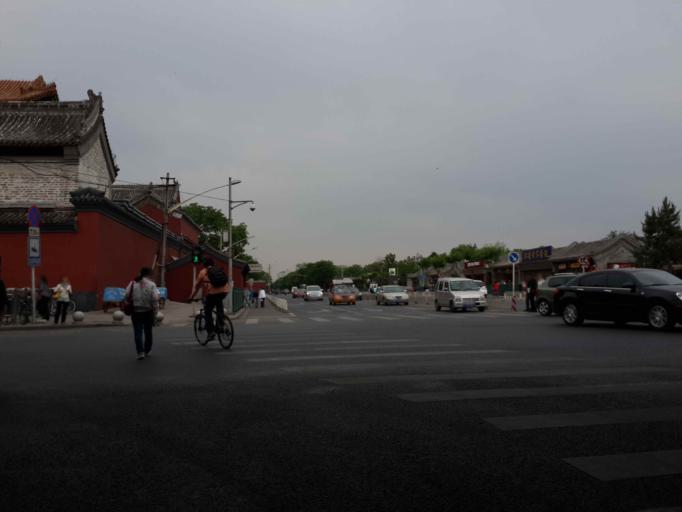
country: CN
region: Beijing
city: Jingshan
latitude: 39.9481
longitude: 116.4106
